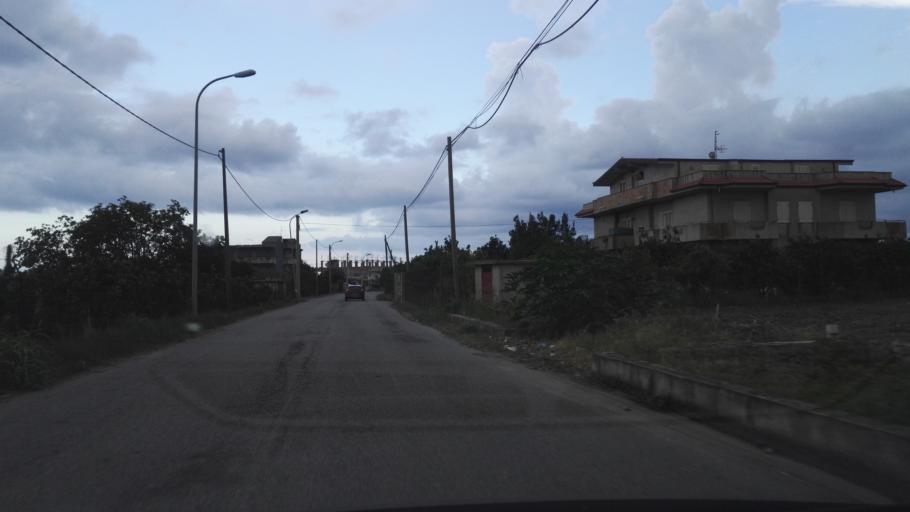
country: IT
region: Calabria
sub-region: Provincia di Reggio Calabria
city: Caulonia Marina
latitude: 38.3528
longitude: 16.4719
